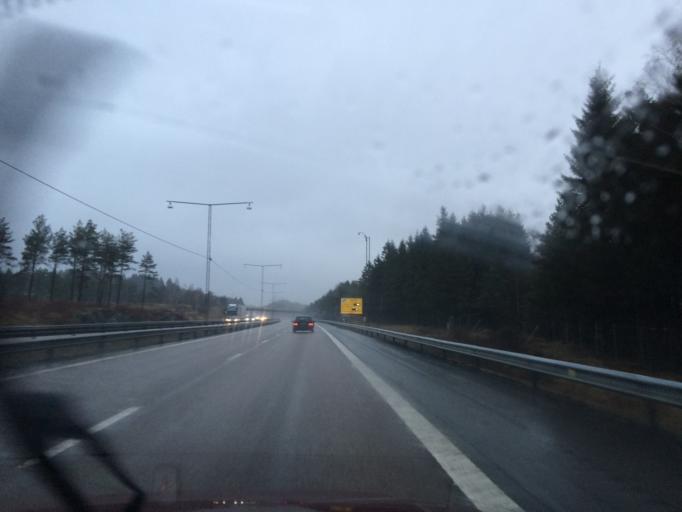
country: SE
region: Vaestra Goetaland
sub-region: Molndal
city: Lindome
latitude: 57.5686
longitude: 12.0564
